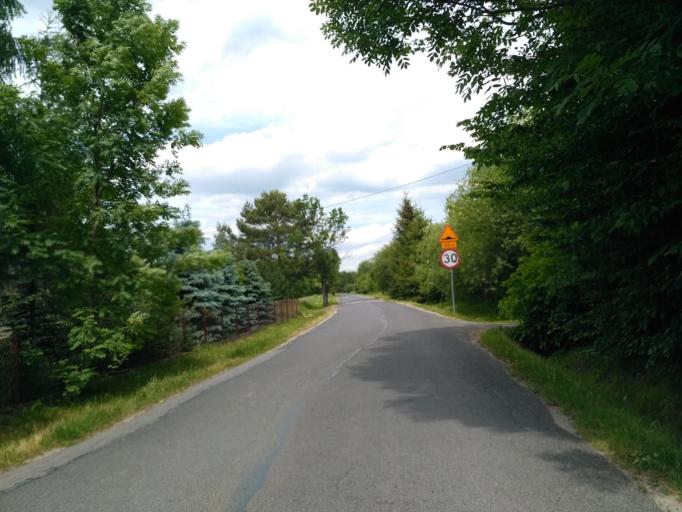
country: PL
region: Subcarpathian Voivodeship
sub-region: Powiat krosnienski
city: Chorkowka
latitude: 49.6907
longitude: 21.7049
